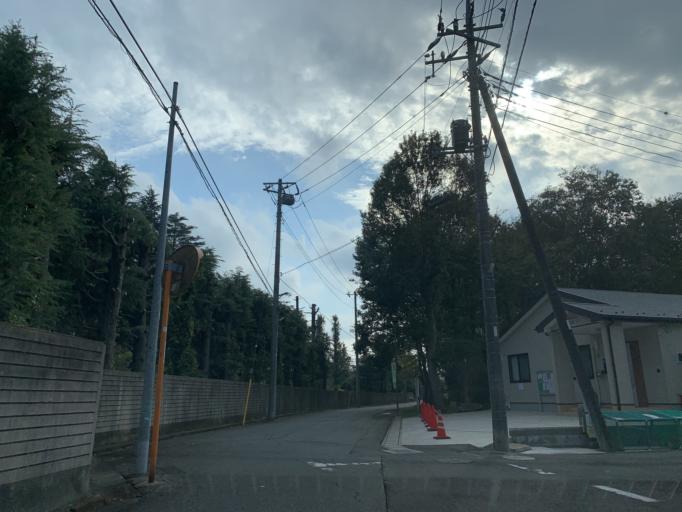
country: JP
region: Chiba
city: Nagareyama
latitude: 35.9084
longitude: 139.9136
